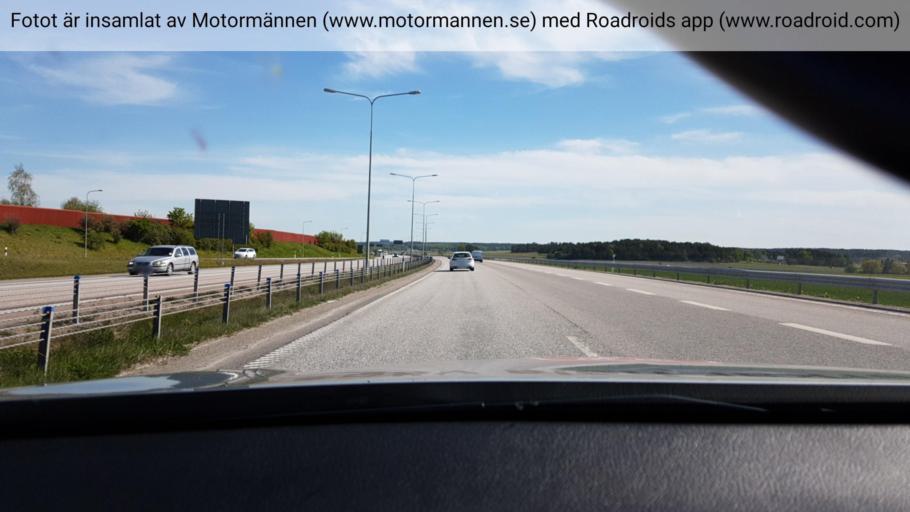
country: SE
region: Uppsala
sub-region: Uppsala Kommun
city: Saevja
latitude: 59.8329
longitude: 17.7348
